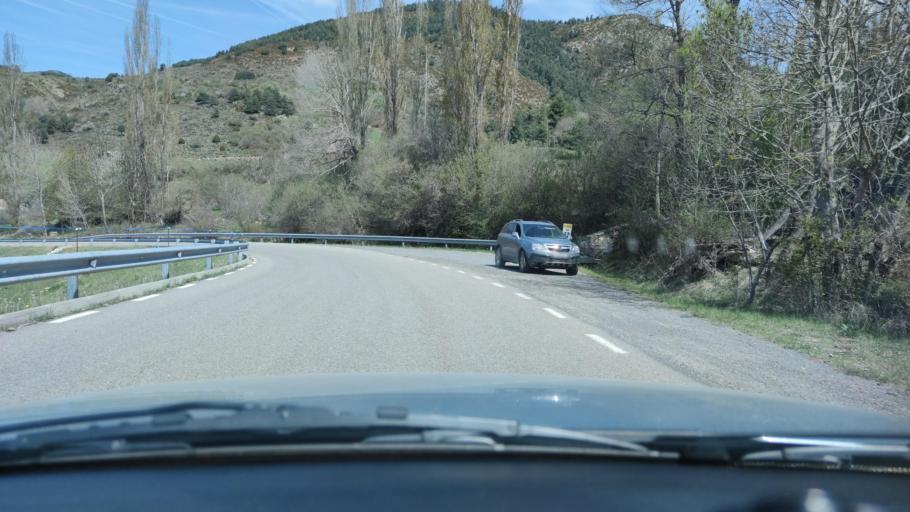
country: ES
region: Catalonia
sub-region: Provincia de Lleida
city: Coll de Nargo
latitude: 42.2837
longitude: 1.2202
